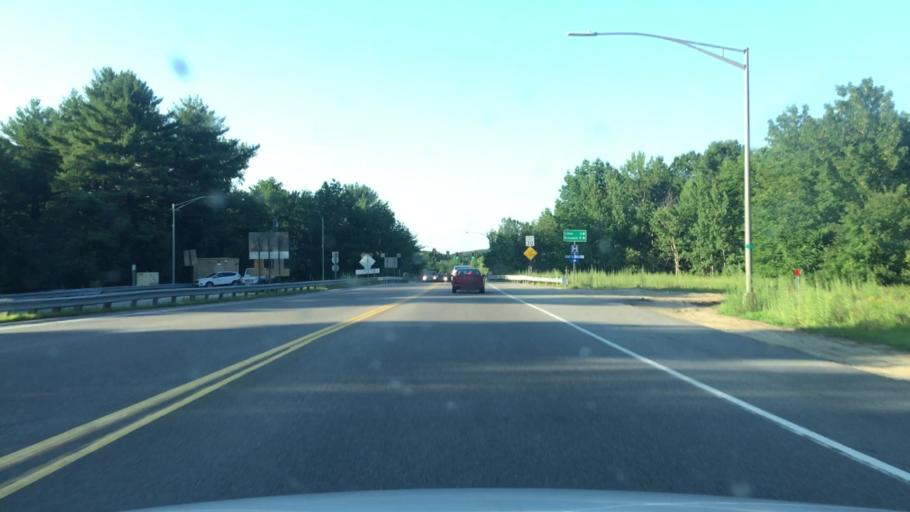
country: US
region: Maine
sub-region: Androscoggin County
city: Lewiston
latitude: 44.0734
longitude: -70.1838
